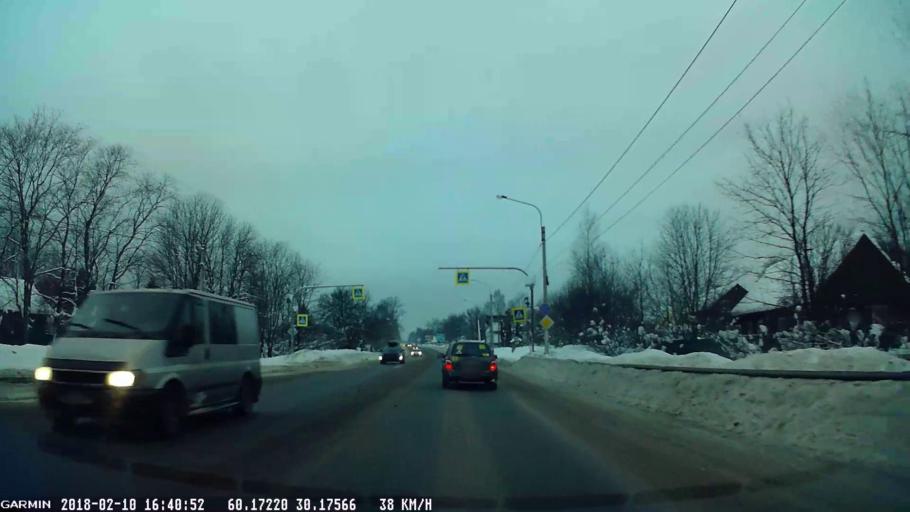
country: RU
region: Leningrad
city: Sertolovo
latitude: 60.1622
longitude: 30.1834
